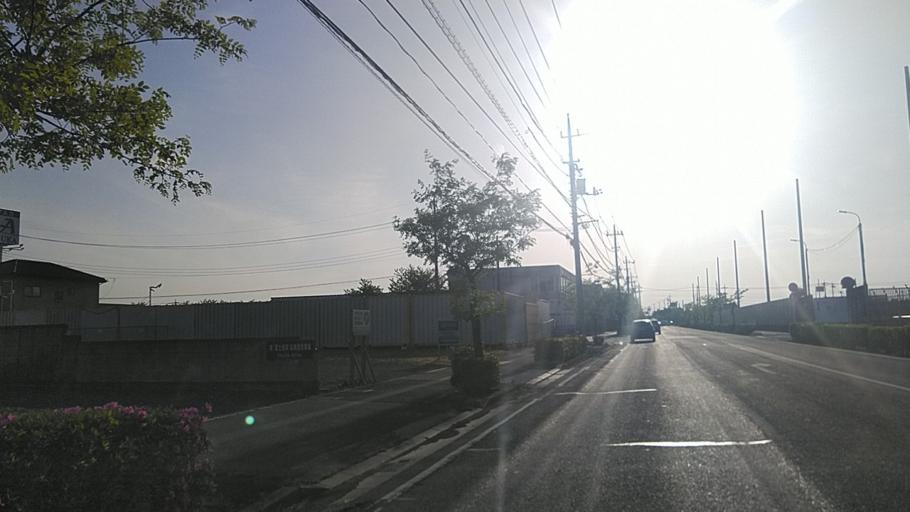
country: JP
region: Gunma
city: Ota
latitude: 36.2752
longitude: 139.3689
